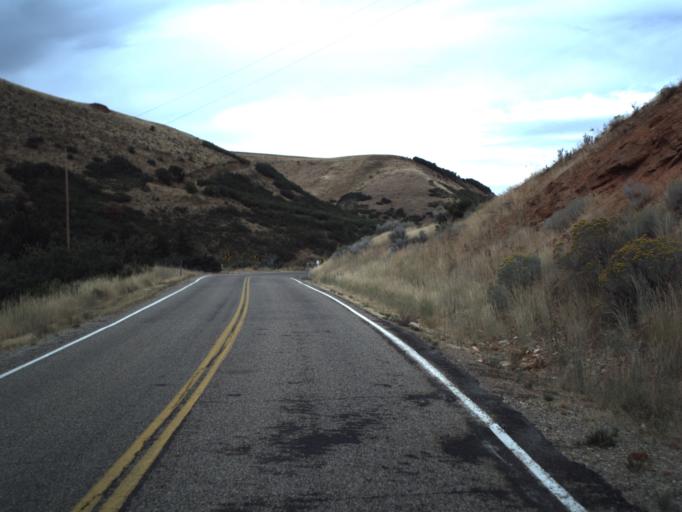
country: US
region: Utah
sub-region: Morgan County
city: Morgan
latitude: 40.9378
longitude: -111.6393
